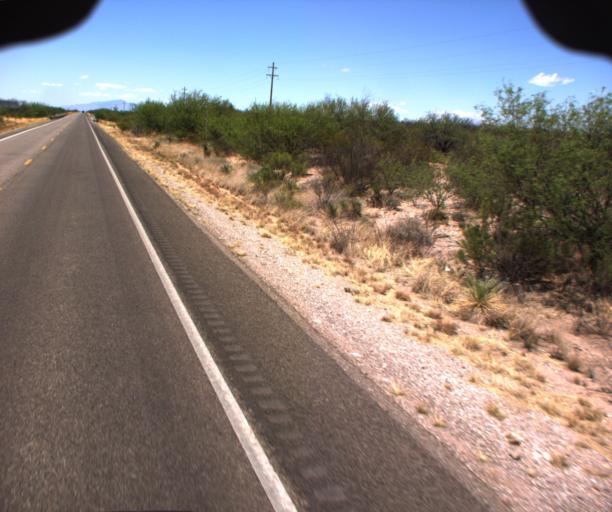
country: US
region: Arizona
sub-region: Cochise County
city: Tombstone
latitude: 31.7585
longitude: -110.1091
